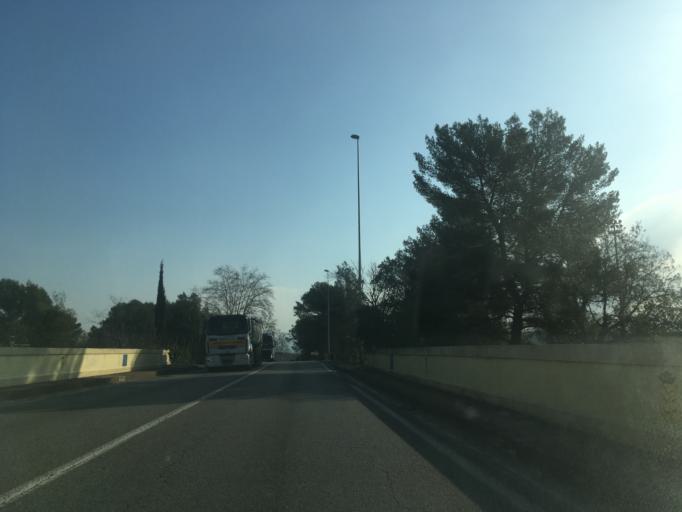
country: FR
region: Provence-Alpes-Cote d'Azur
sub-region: Departement du Var
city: Le Cannet-des-Maures
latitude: 43.3918
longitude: 6.3443
